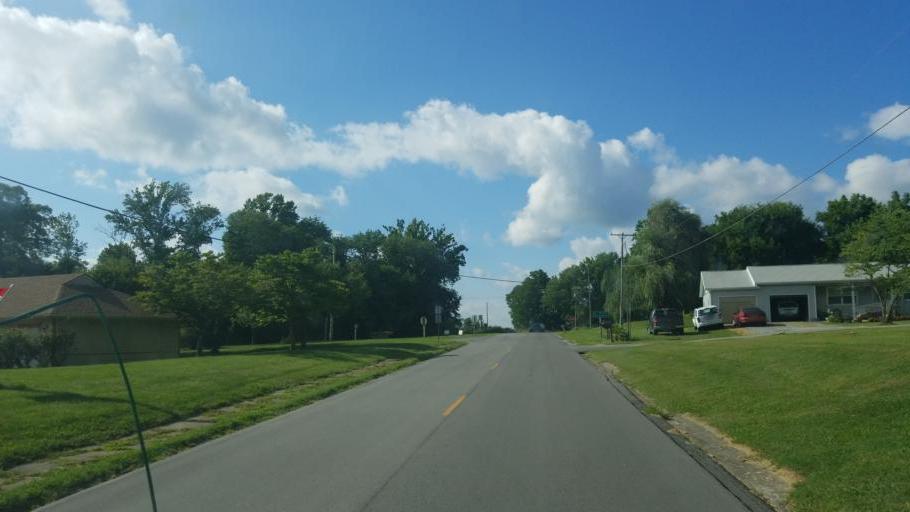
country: US
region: Illinois
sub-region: Union County
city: Cobden
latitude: 37.5754
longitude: -89.3206
